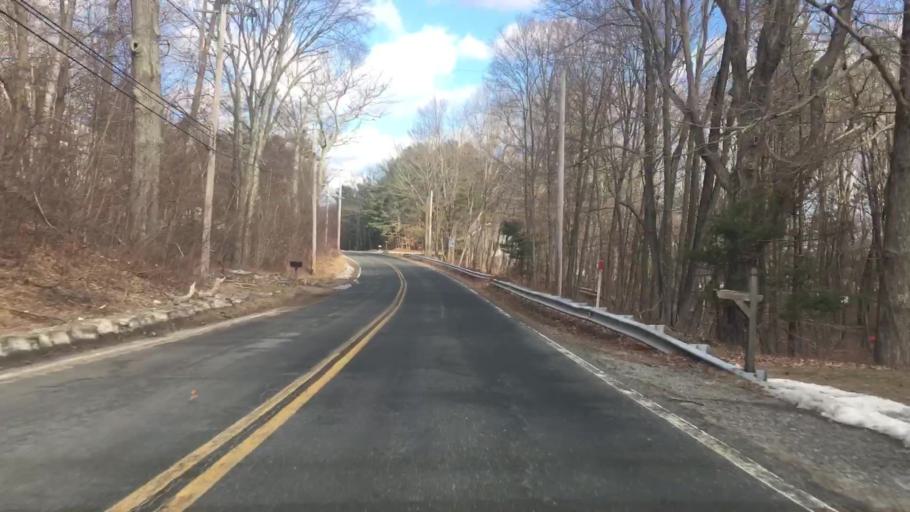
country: US
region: Massachusetts
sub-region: Hampden County
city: Wales
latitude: 42.0534
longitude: -72.2272
